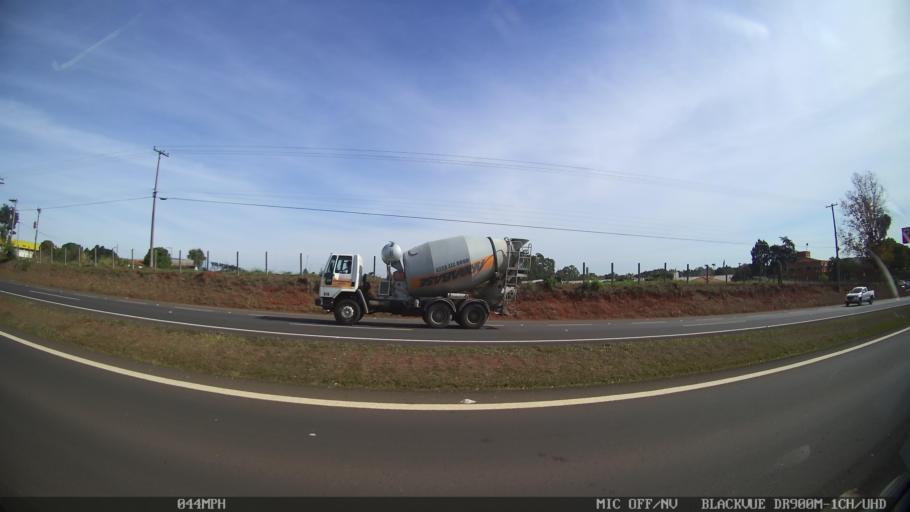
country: BR
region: Sao Paulo
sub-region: Piracicaba
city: Piracicaba
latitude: -22.7764
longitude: -47.6503
